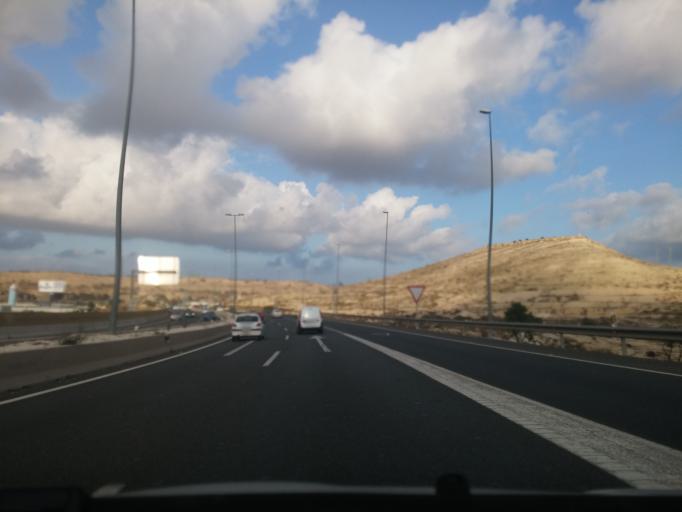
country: ES
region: Valencia
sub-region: Provincia de Alicante
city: Alicante
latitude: 38.3841
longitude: -0.4854
